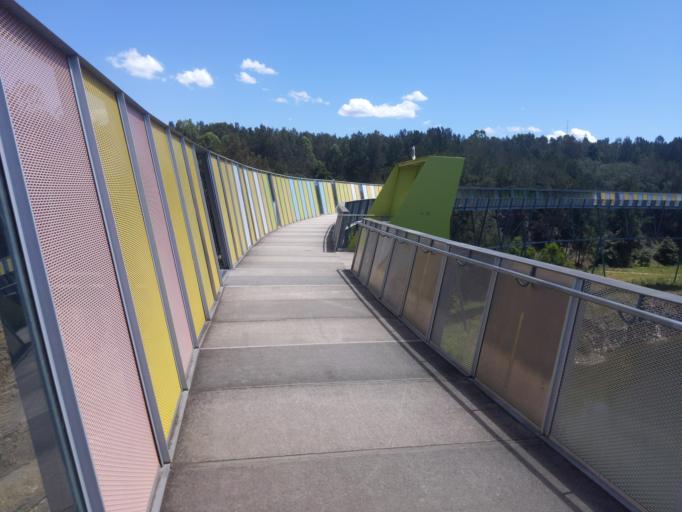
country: AU
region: New South Wales
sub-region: Canada Bay
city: Concord West
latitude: -33.8411
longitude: 151.0708
